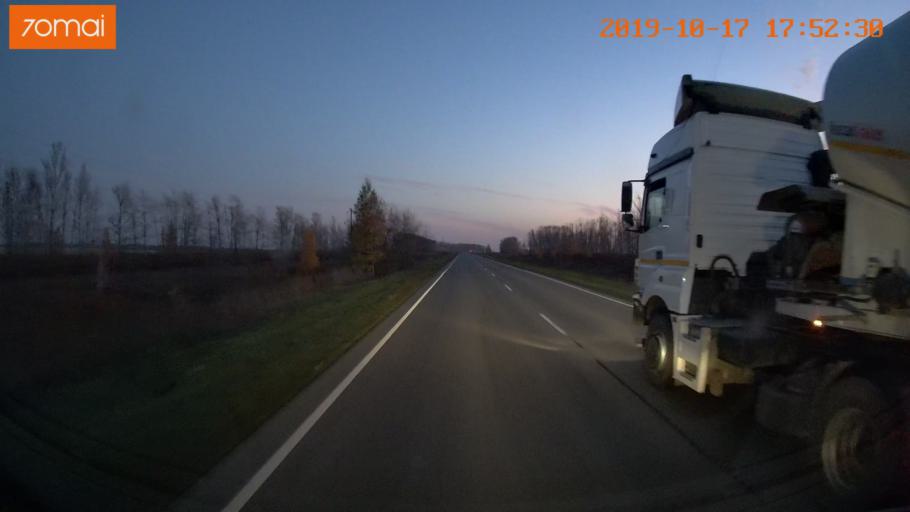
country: RU
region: Tula
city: Kurkino
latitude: 53.6339
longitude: 38.6835
